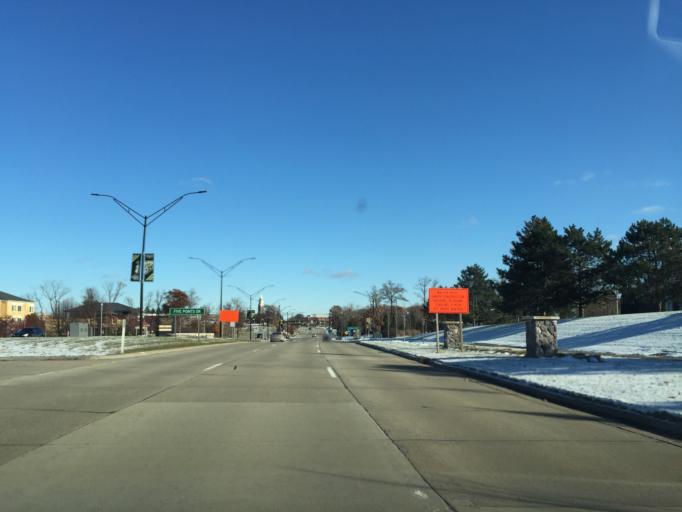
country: US
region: Michigan
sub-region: Oakland County
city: Auburn Hills
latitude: 42.6722
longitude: -83.2259
